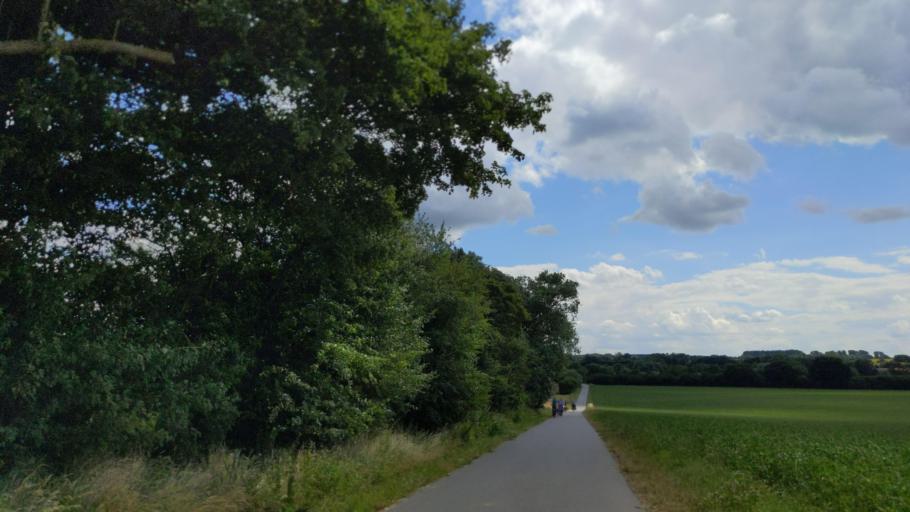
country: DE
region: Mecklenburg-Vorpommern
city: Kalkhorst
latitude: 54.0071
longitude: 11.0791
